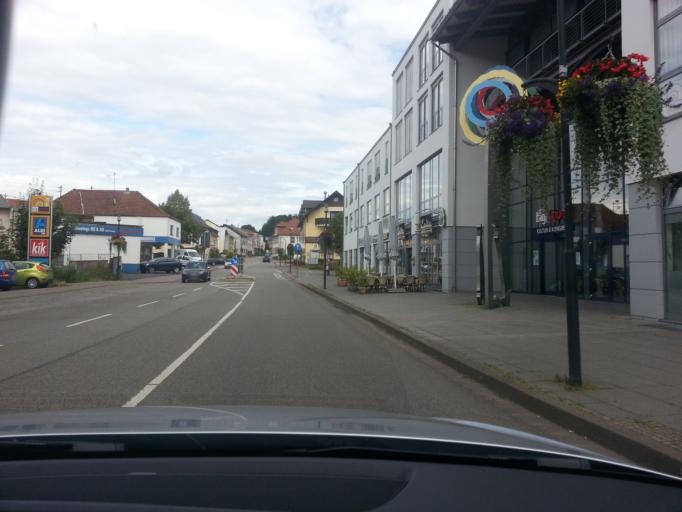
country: DE
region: Saarland
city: Eppelborn
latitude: 49.4073
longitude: 6.9691
